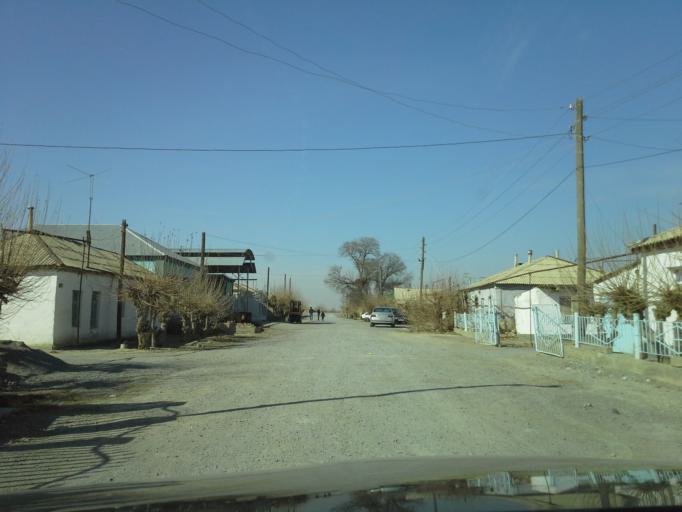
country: TM
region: Ahal
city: Abadan
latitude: 38.1068
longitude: 58.0324
